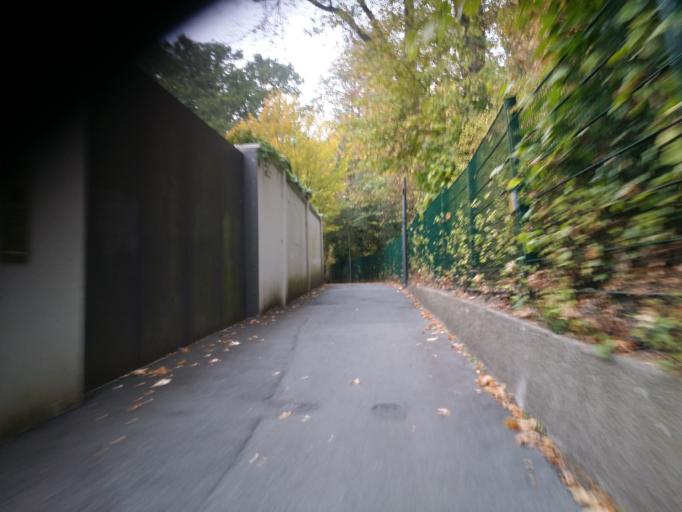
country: DE
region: Lower Saxony
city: Lemwerder
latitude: 53.1645
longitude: 8.6319
